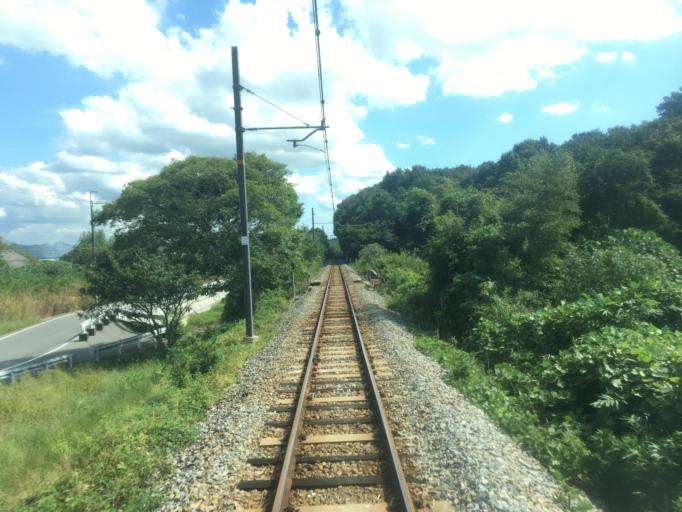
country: JP
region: Hyogo
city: Ono
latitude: 34.8296
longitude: 134.9249
